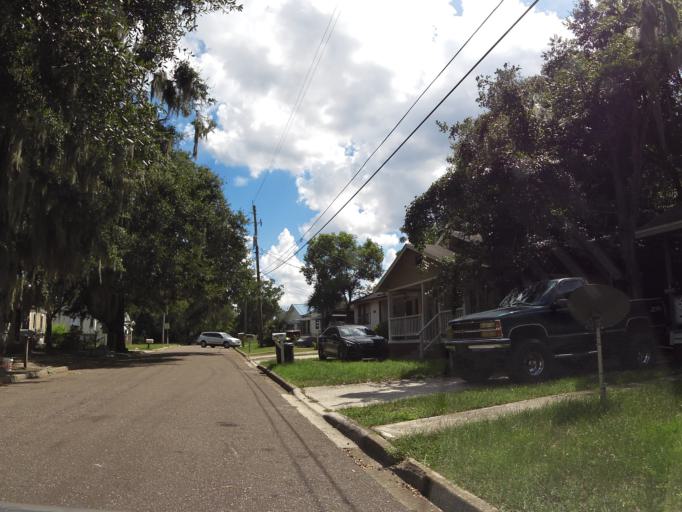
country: US
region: Florida
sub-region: Duval County
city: Jacksonville
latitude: 30.3874
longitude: -81.6468
